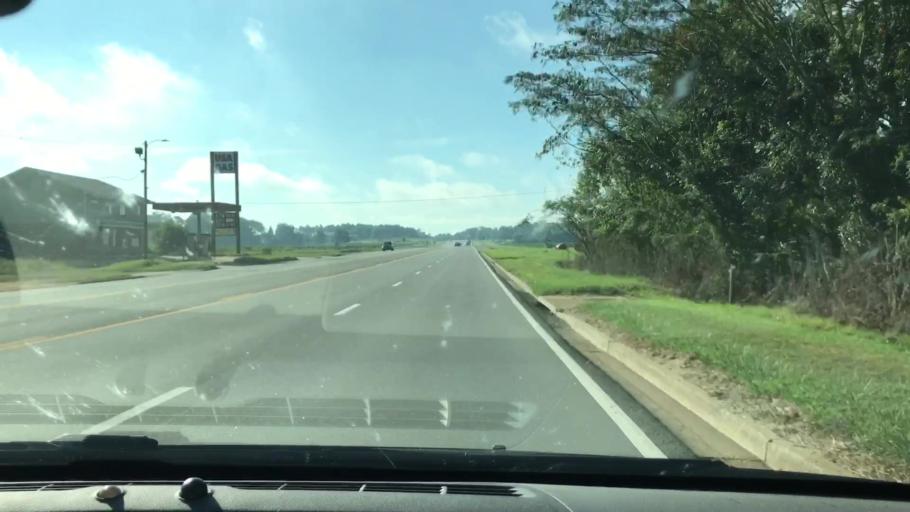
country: US
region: Georgia
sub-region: Terrell County
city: Dawson
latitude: 31.7176
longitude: -84.3473
